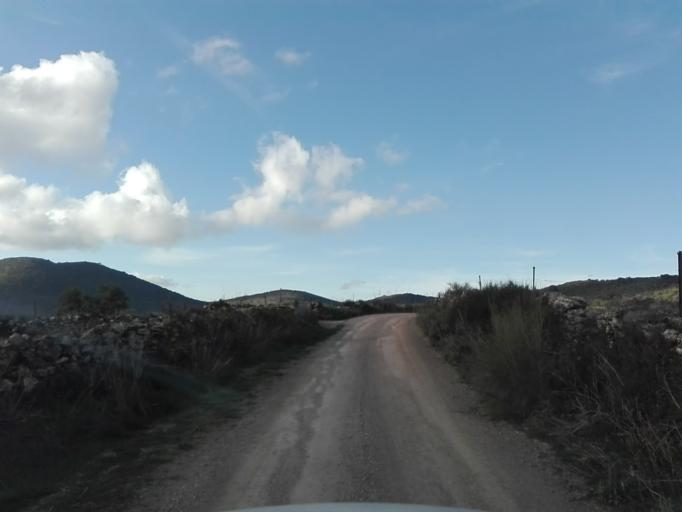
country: ES
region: Extremadura
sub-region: Provincia de Badajoz
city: Trasierra
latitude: 38.1921
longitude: -5.9855
